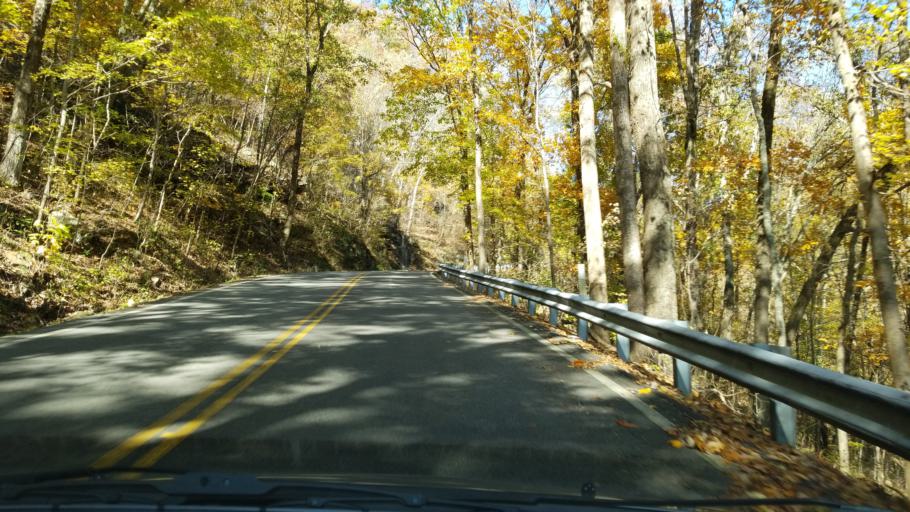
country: US
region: Tennessee
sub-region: Hamilton County
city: Falling Water
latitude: 35.2137
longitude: -85.2609
